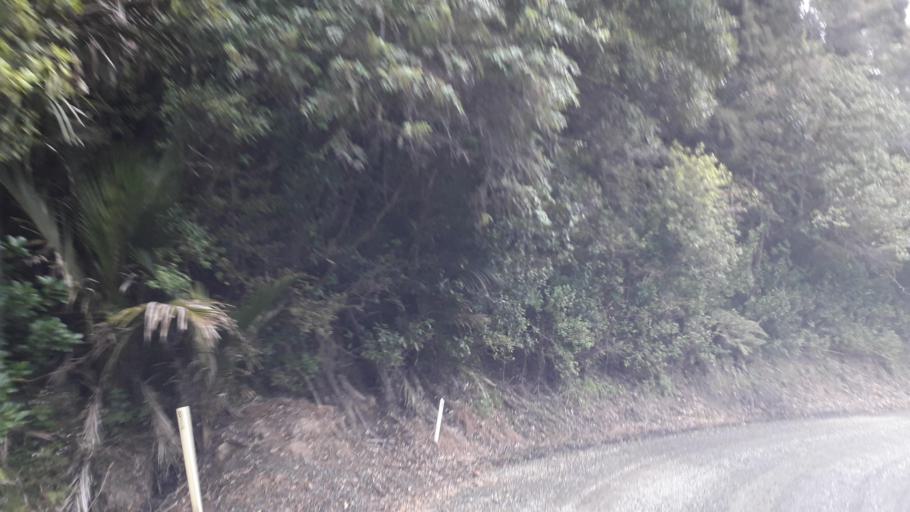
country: NZ
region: Northland
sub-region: Far North District
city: Kerikeri
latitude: -35.1319
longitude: 173.7192
